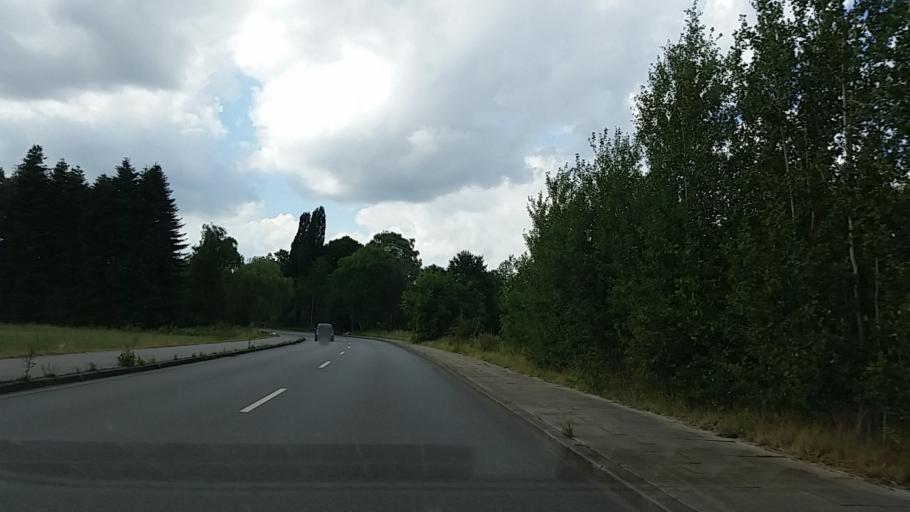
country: DE
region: Schleswig-Holstein
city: Barmstedt
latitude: 53.7824
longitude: 9.7650
